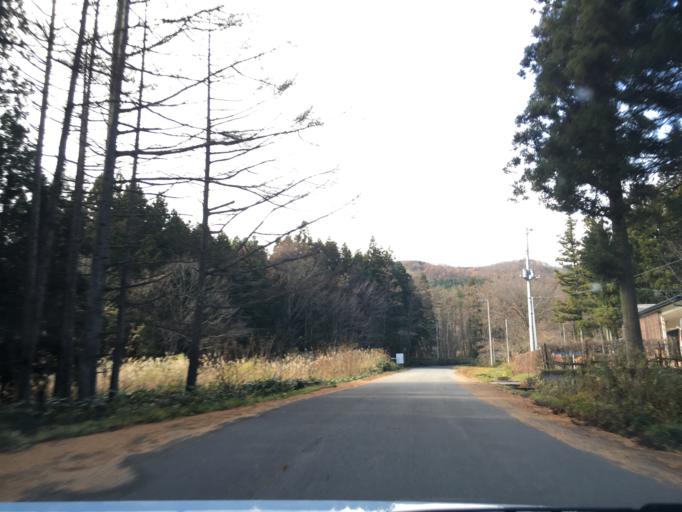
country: JP
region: Fukushima
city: Inawashiro
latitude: 37.4521
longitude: 140.0114
